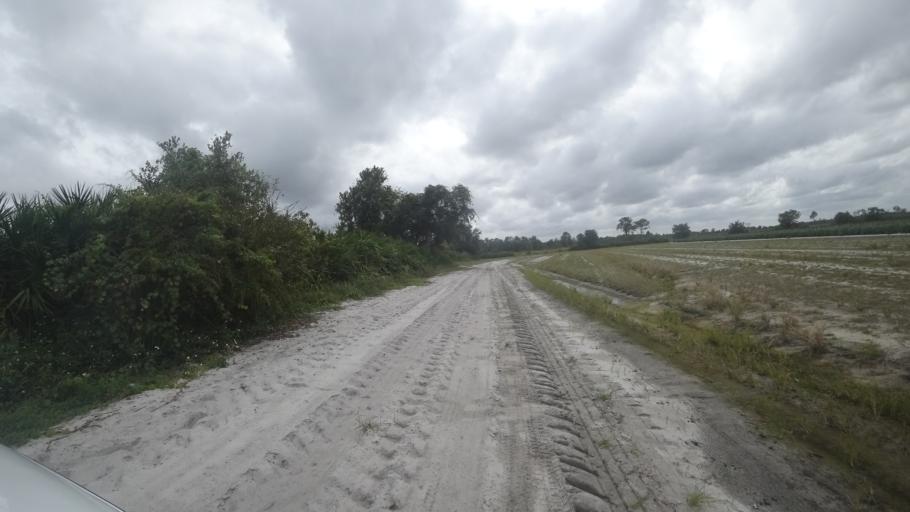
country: US
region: Florida
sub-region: Hillsborough County
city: Wimauma
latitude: 27.5607
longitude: -82.1295
